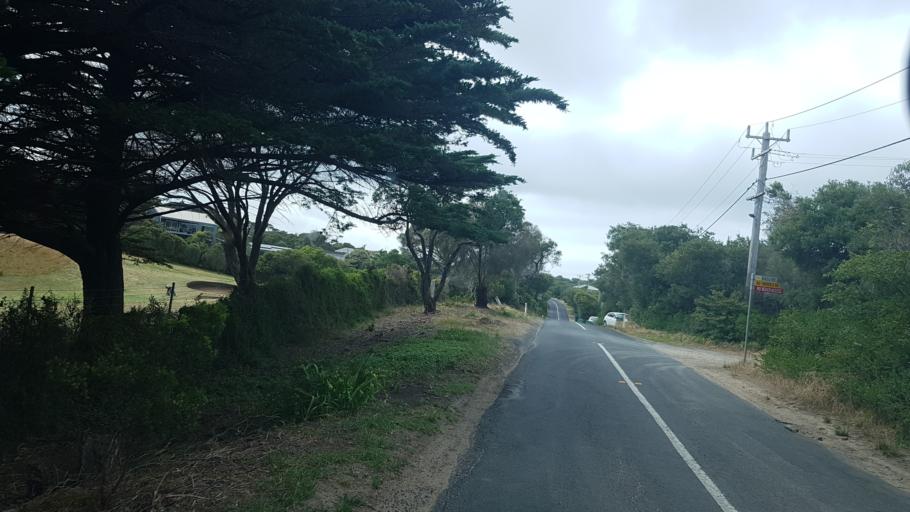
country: AU
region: Victoria
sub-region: Mornington Peninsula
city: Sorrento
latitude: -38.3271
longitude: 144.7055
